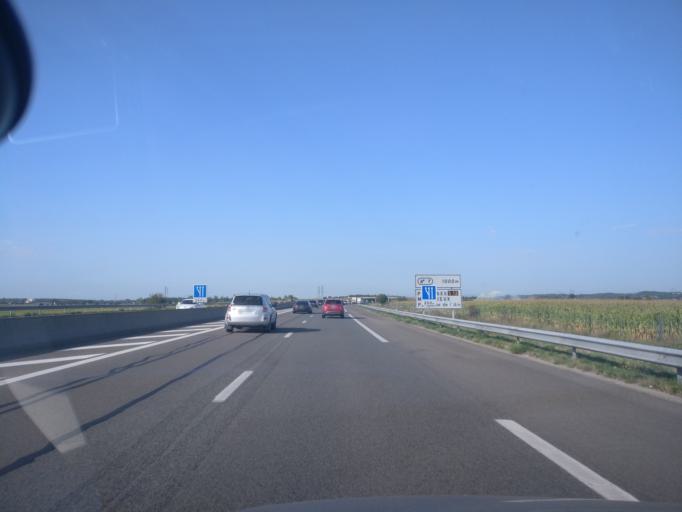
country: FR
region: Rhone-Alpes
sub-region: Departement de l'Ain
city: Meximieux
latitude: 45.8666
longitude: 5.1902
